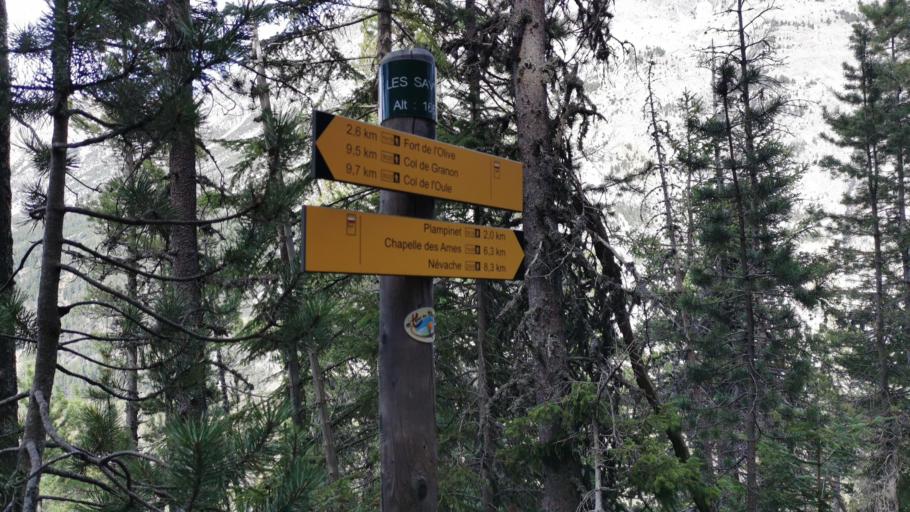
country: IT
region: Piedmont
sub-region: Provincia di Torino
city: Bardonecchia
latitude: 45.0085
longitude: 6.6471
